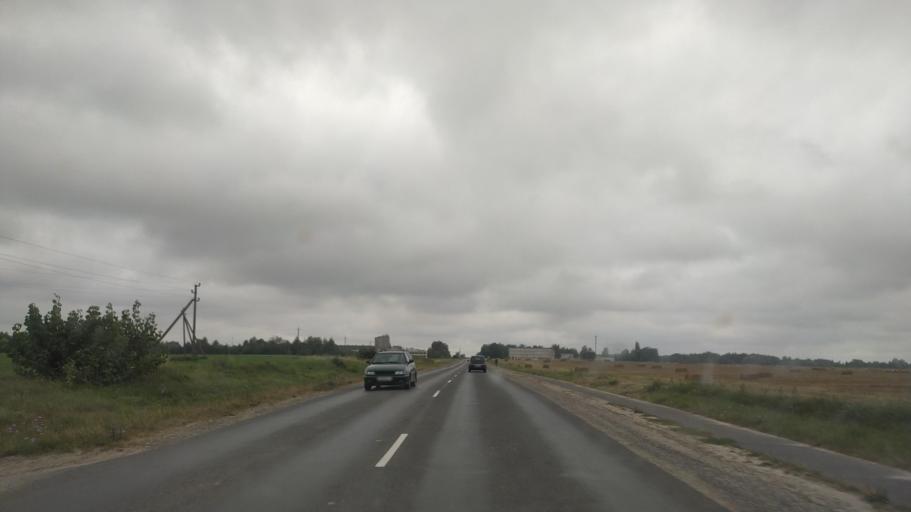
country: BY
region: Brest
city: Byaroza
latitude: 52.5482
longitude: 24.9488
